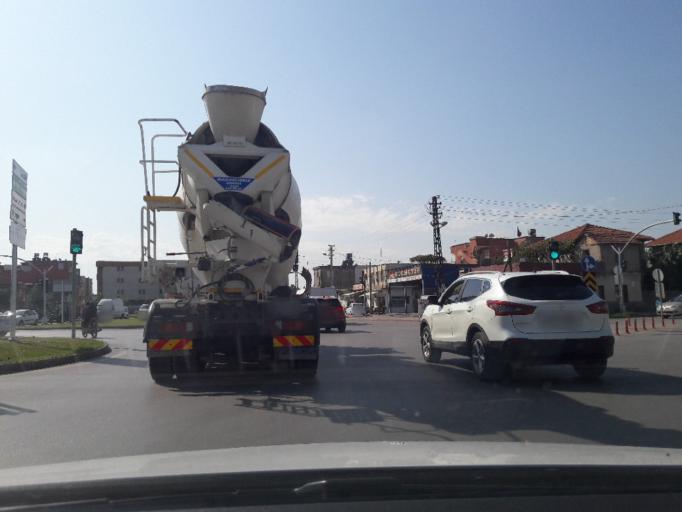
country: TR
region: Adana
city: Seyhan
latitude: 36.9953
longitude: 35.3004
